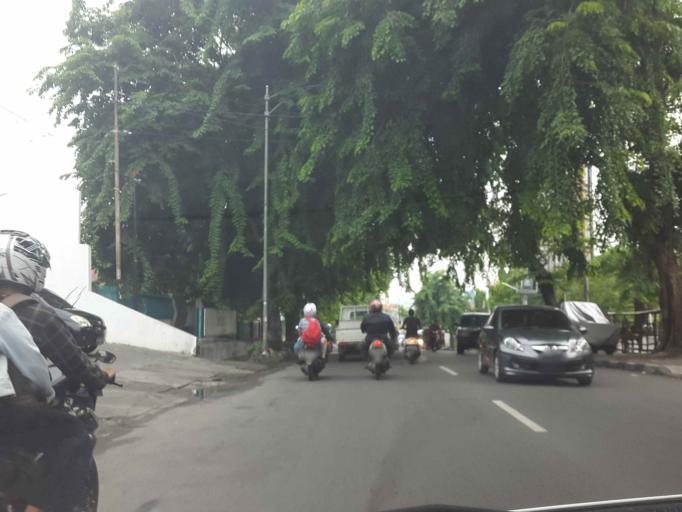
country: ID
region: Central Java
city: Semarang
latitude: -7.0045
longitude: 110.4273
